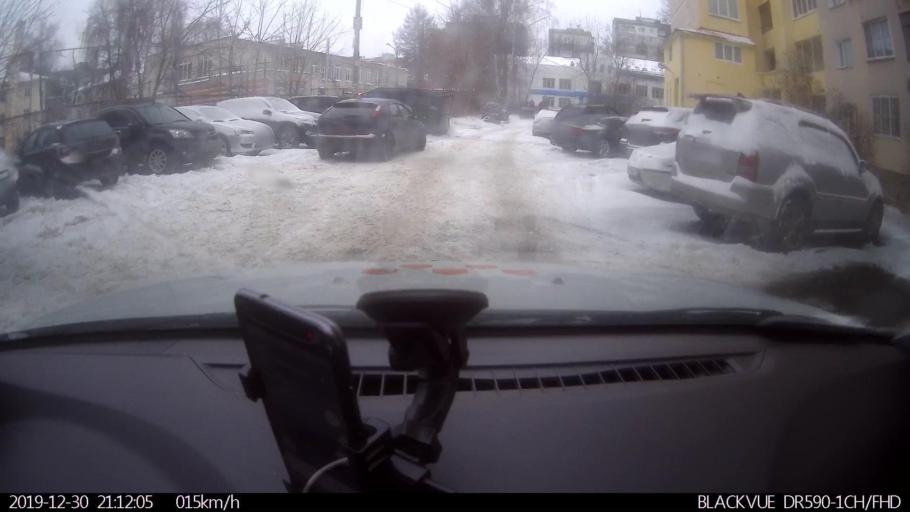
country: RU
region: Nizjnij Novgorod
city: Nizhniy Novgorod
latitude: 56.3112
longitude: 44.0287
